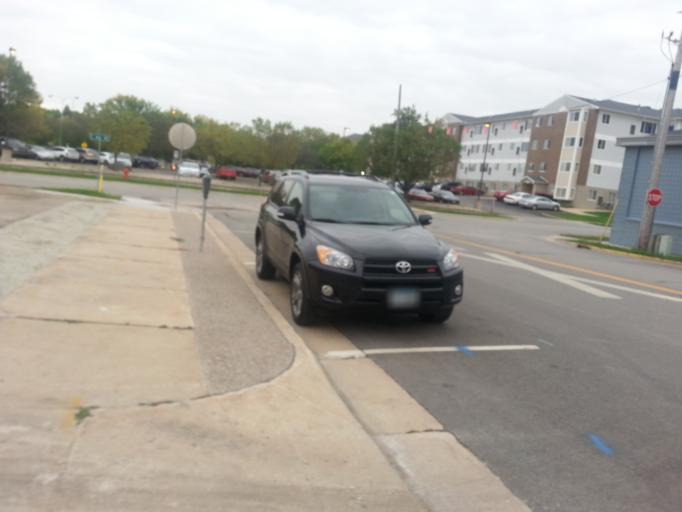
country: US
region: Minnesota
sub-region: Olmsted County
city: Rochester
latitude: 44.0254
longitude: -92.4620
